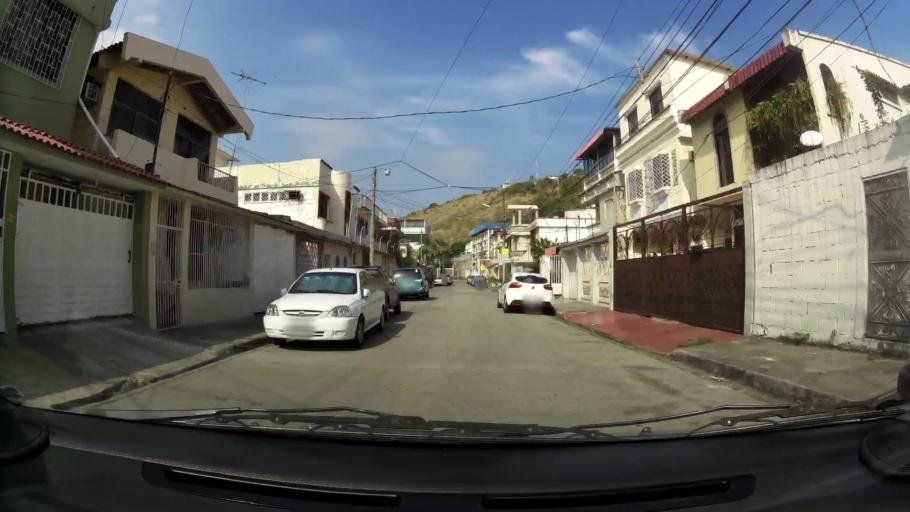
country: EC
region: Guayas
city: Guayaquil
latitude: -2.1807
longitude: -79.9109
